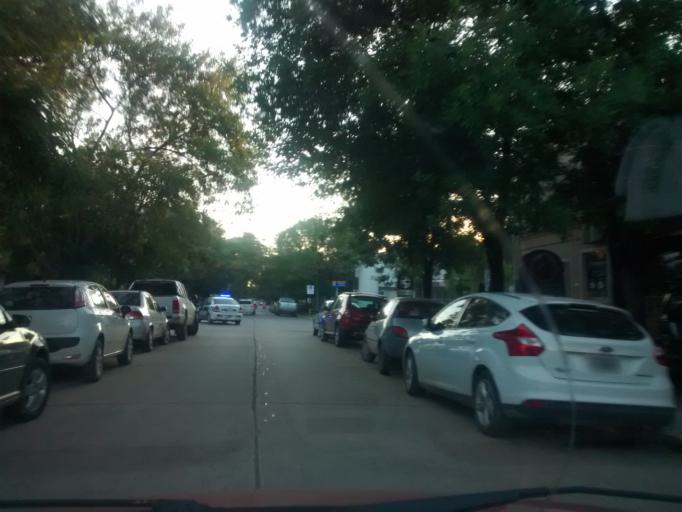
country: AR
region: Chaco
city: Resistencia
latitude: -27.4447
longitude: -58.9844
